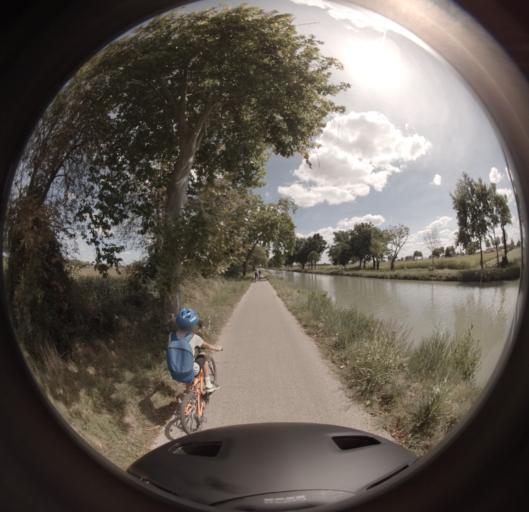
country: FR
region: Midi-Pyrenees
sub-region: Departement du Tarn-et-Garonne
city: Saint-Porquier
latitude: 44.0282
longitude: 1.1470
